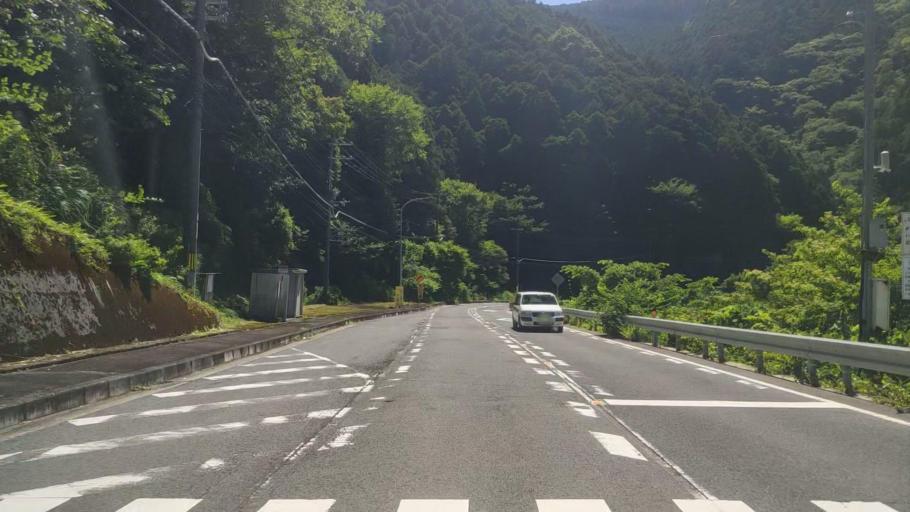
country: JP
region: Nara
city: Yoshino-cho
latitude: 34.3183
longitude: 135.9719
